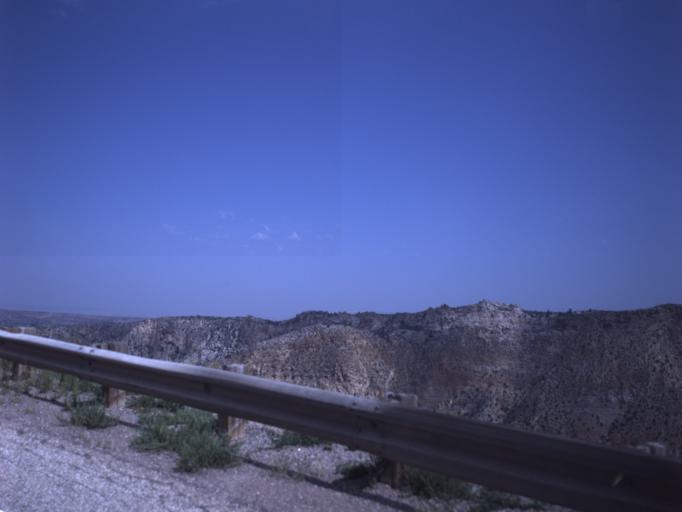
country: US
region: Utah
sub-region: Daggett County
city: Manila
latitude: 40.9110
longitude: -109.6956
